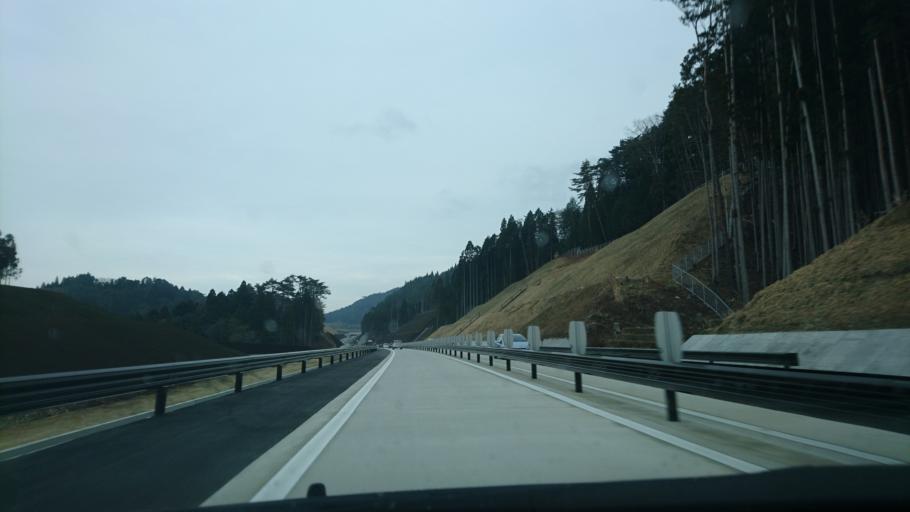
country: JP
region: Iwate
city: Ofunato
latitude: 38.9604
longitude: 141.6249
